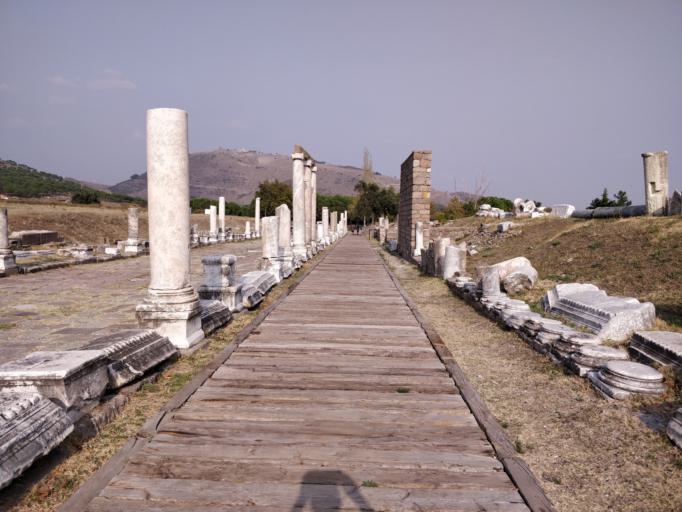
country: TR
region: Izmir
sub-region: Bergama
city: Bergama
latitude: 39.1190
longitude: 27.1670
